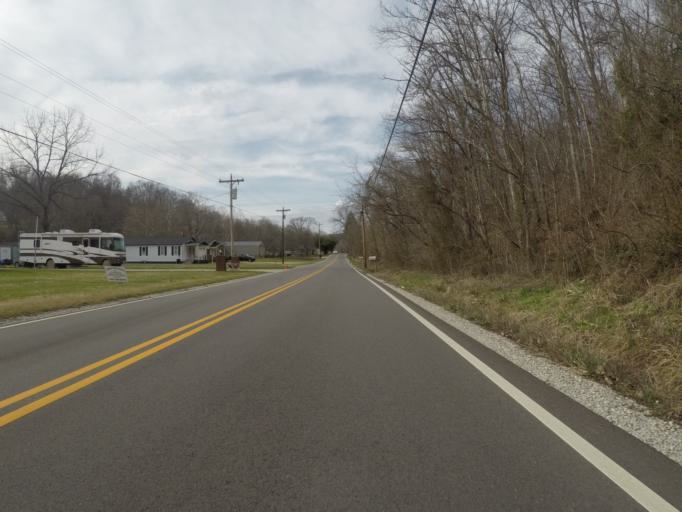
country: US
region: Ohio
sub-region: Lawrence County
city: Burlington
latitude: 38.4391
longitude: -82.4987
